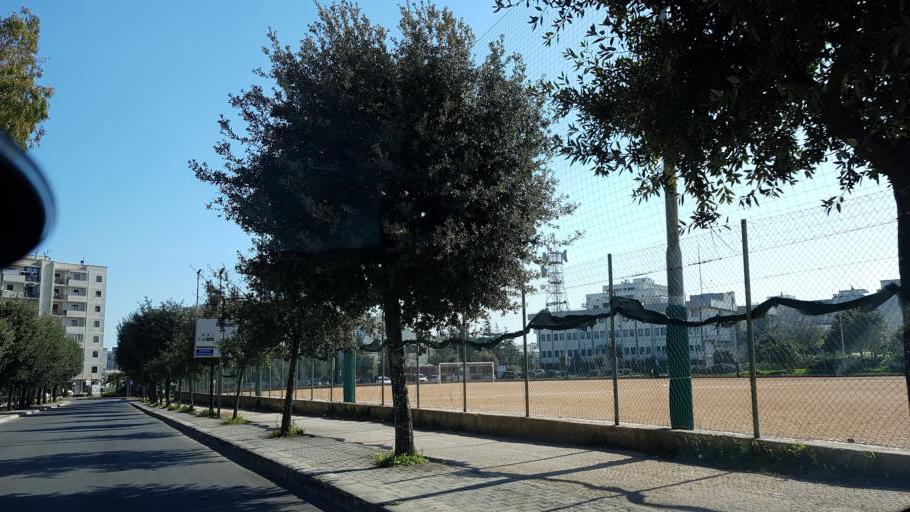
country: IT
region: Apulia
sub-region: Provincia di Brindisi
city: Ostuni
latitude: 40.7220
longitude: 17.5816
